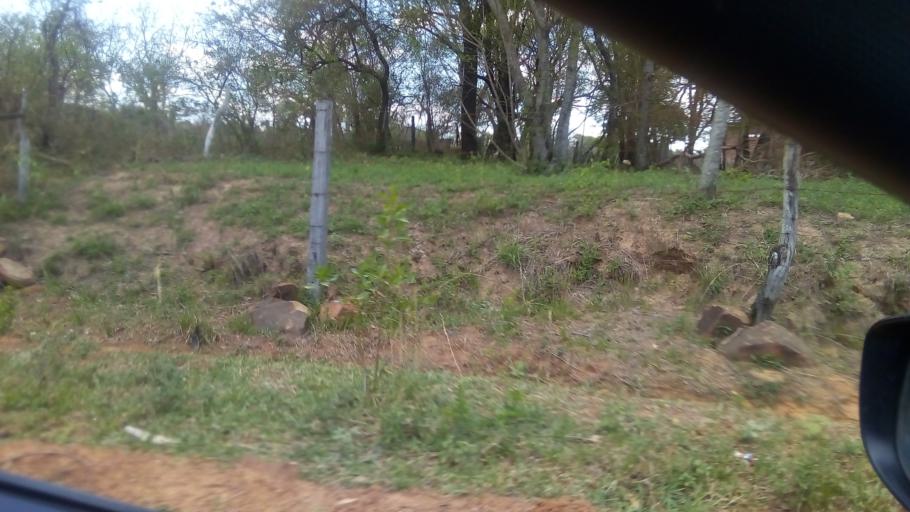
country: PY
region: Cordillera
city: Arroyos y Esteros
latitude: -24.9867
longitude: -57.2099
